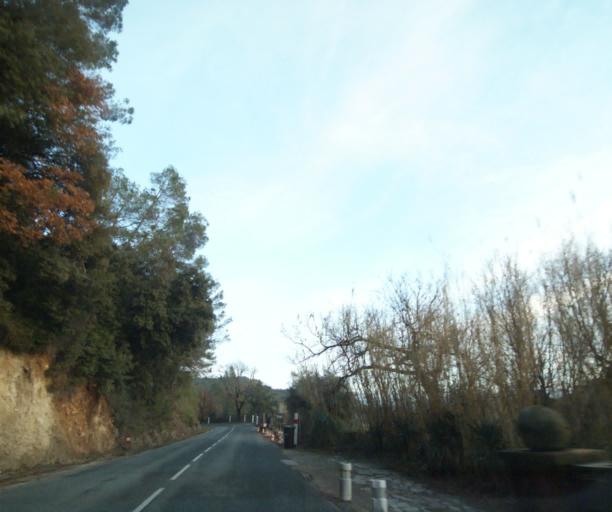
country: FR
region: Provence-Alpes-Cote d'Azur
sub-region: Departement du Var
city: Trans-en-Provence
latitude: 43.4976
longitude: 6.5027
